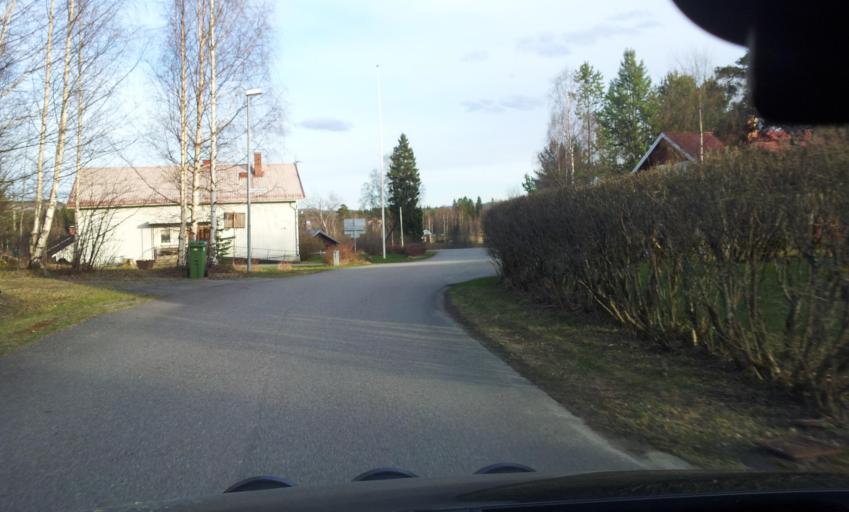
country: SE
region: Vaesternorrland
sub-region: Ange Kommun
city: Ange
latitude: 62.1848
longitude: 15.6505
